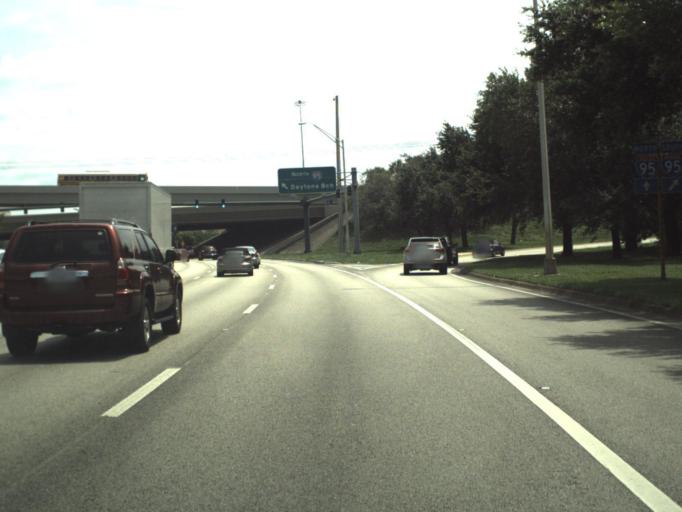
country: US
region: Florida
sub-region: Palm Beach County
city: North Palm Beach
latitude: 26.8385
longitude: -80.1032
